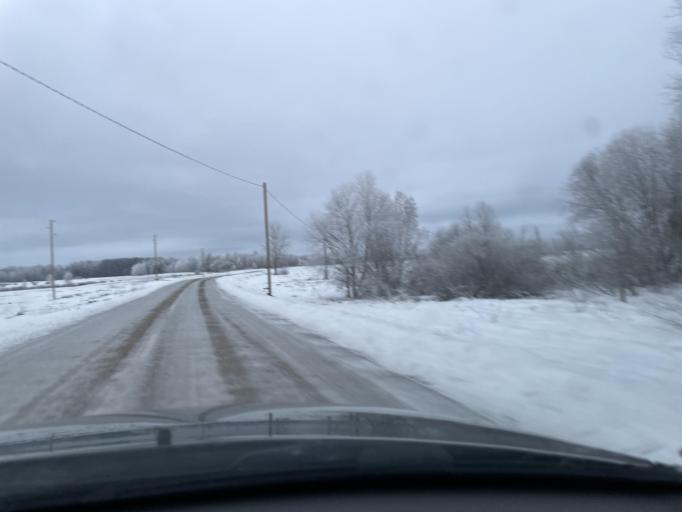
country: LV
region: Ludzas Rajons
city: Ludza
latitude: 56.4604
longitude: 27.5697
